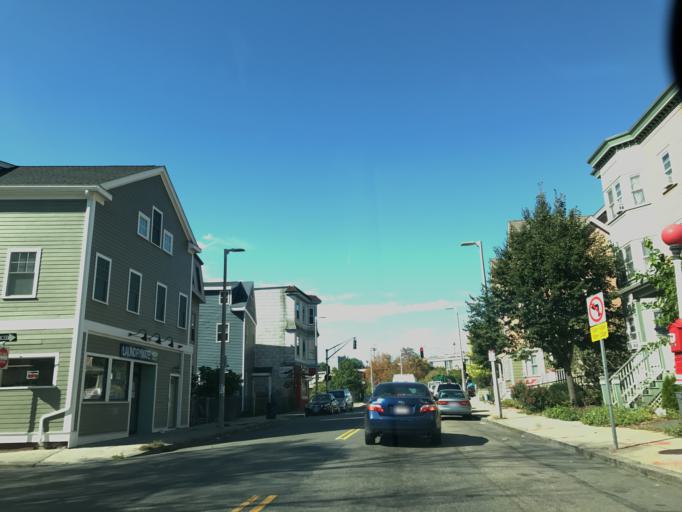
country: US
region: Massachusetts
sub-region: Norfolk County
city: Brookline
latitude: 42.3261
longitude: -71.1045
